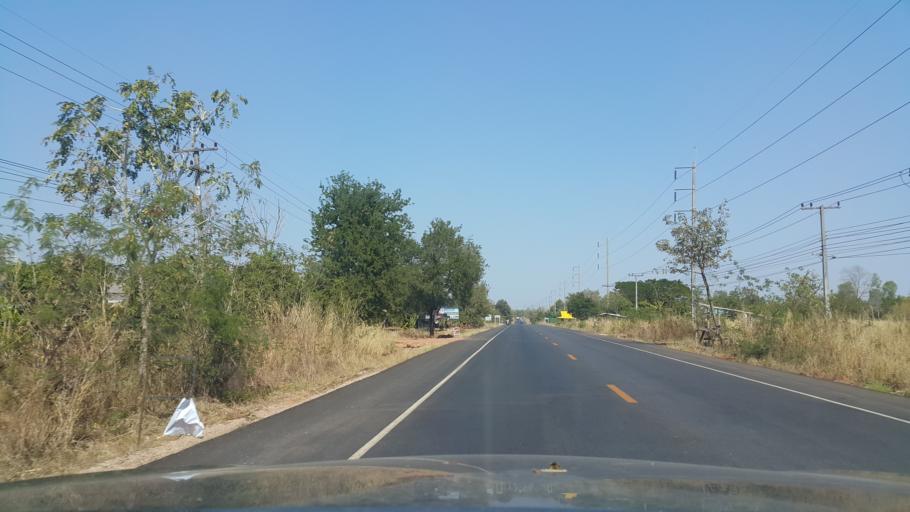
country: TH
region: Changwat Udon Thani
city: Thung Fon
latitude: 17.5769
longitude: 103.2436
